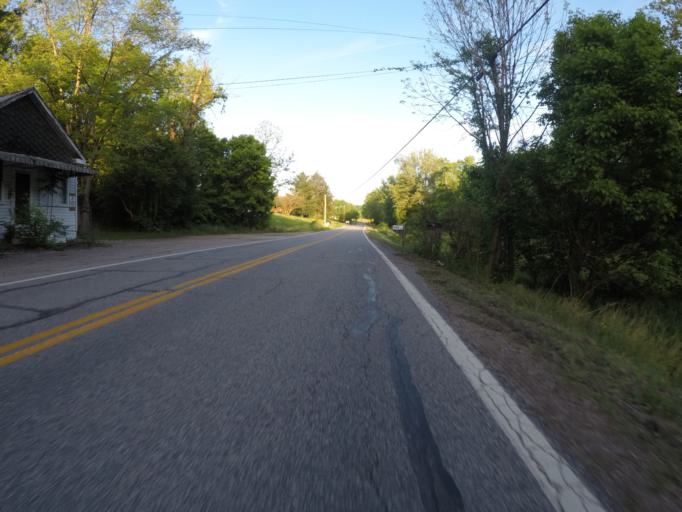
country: US
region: West Virginia
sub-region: Cabell County
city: Huntington
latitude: 38.4885
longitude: -82.4735
